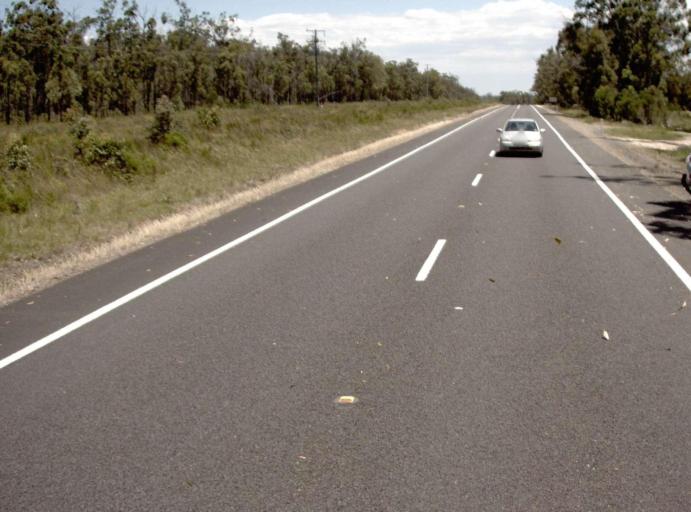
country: AU
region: Victoria
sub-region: East Gippsland
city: Lakes Entrance
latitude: -37.7552
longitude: 148.3099
